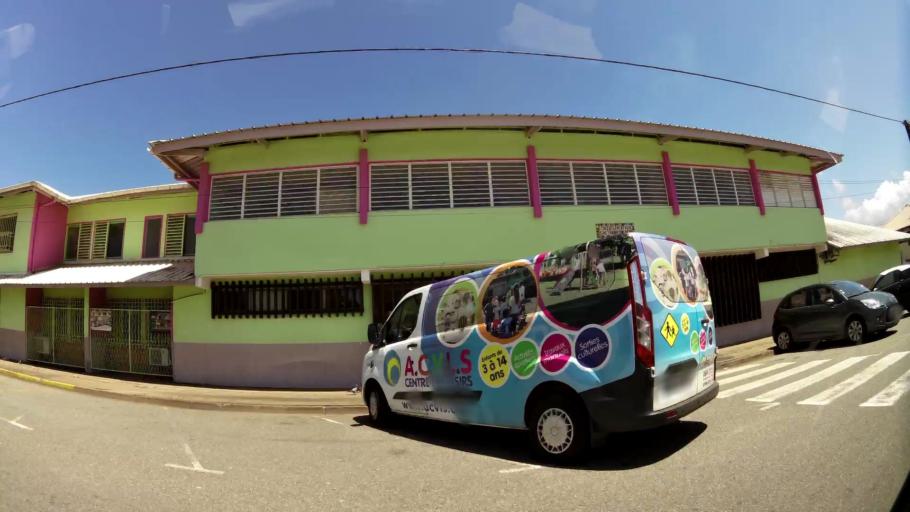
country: GF
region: Guyane
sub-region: Guyane
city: Cayenne
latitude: 4.9336
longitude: -52.3302
